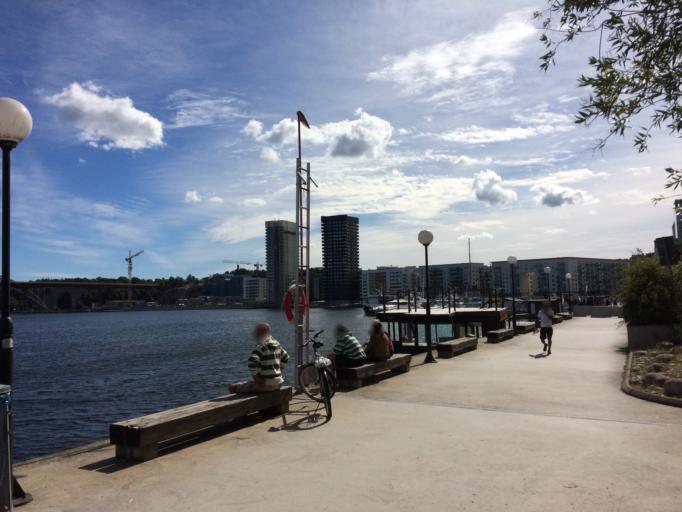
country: SE
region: Stockholm
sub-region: Stockholms Kommun
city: Arsta
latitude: 59.3111
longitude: 18.0324
